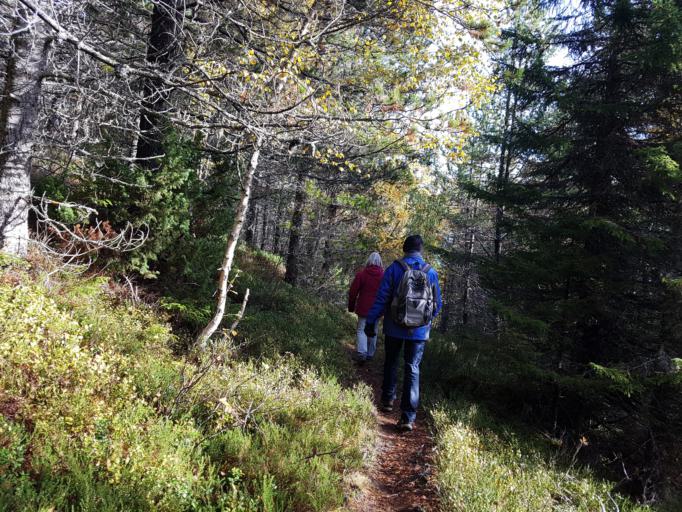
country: NO
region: Sor-Trondelag
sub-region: Trondheim
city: Trondheim
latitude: 63.4238
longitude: 10.2863
